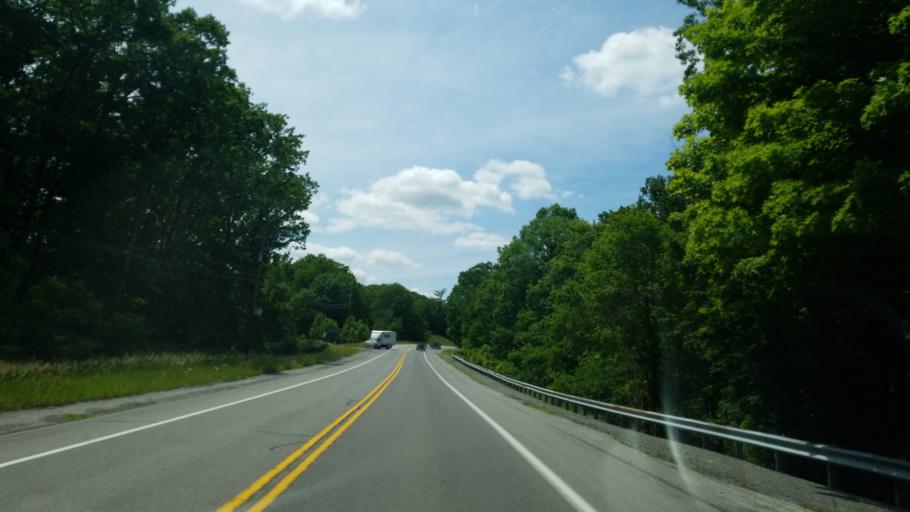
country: US
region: Pennsylvania
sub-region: Blair County
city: Tyrone
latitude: 40.6811
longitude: -78.2590
